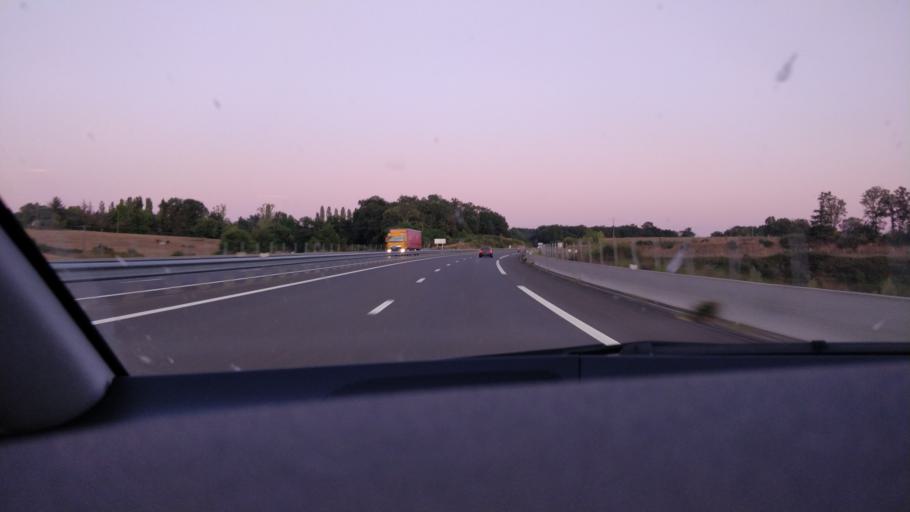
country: FR
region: Poitou-Charentes
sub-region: Departement de la Charente
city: Chabanais
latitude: 45.8684
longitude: 0.7120
